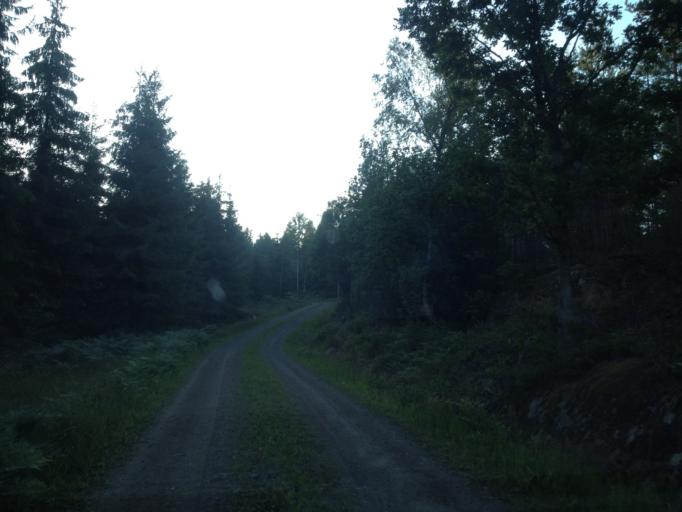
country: SE
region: Kalmar
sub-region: Vasterviks Kommun
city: Overum
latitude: 57.9970
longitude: 16.1682
